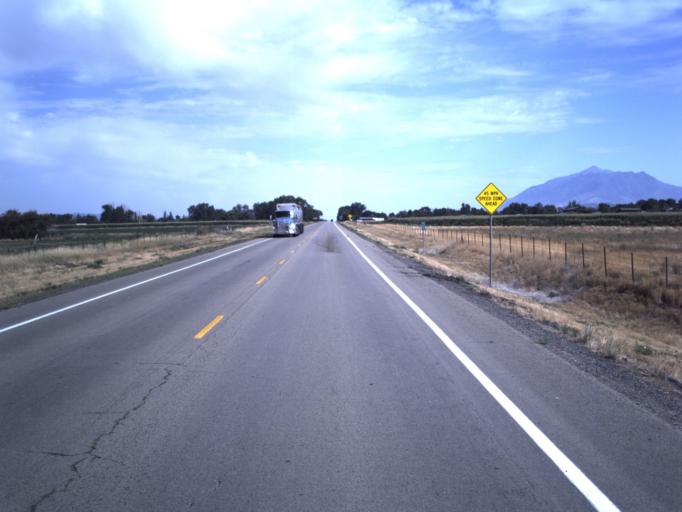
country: US
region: Utah
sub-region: Juab County
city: Nephi
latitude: 39.5440
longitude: -111.8637
